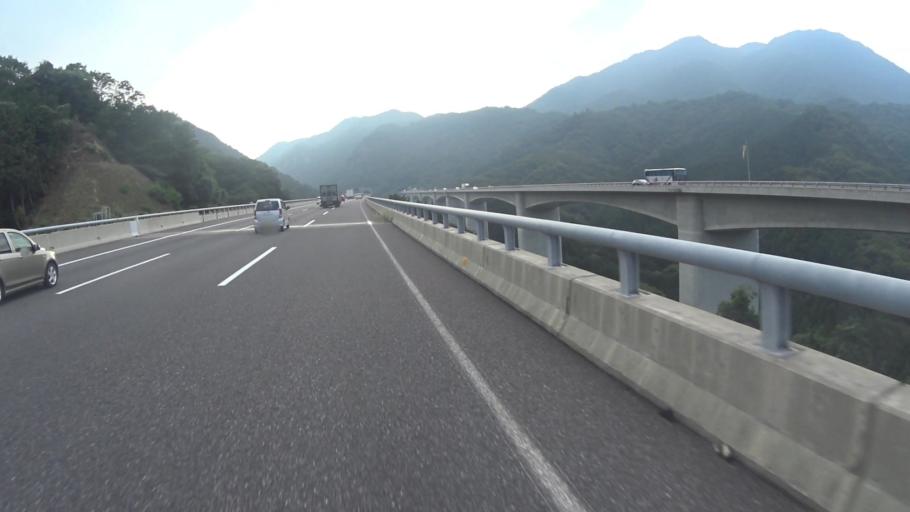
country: JP
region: Mie
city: Kameyama
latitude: 34.9151
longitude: 136.3925
